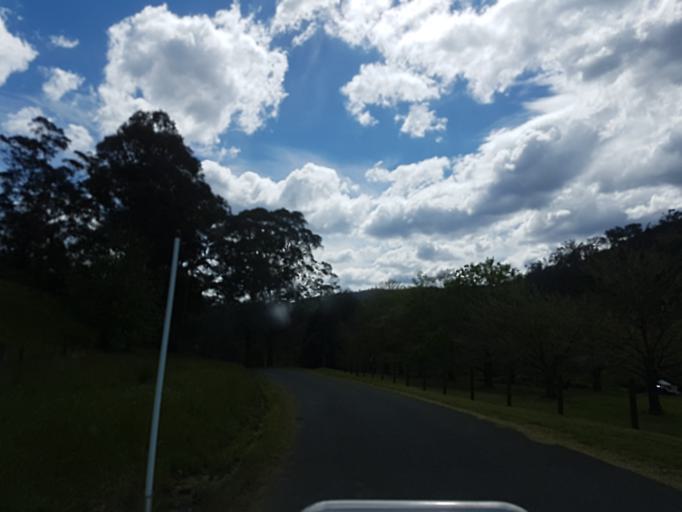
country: AU
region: Victoria
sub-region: East Gippsland
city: Bairnsdale
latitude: -37.4314
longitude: 147.2511
